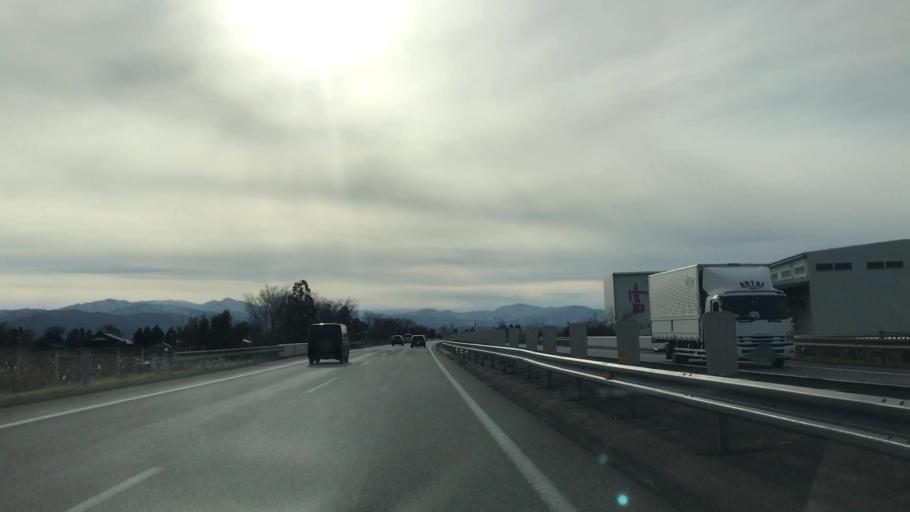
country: JP
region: Toyama
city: Toyama-shi
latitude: 36.6553
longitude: 137.2563
